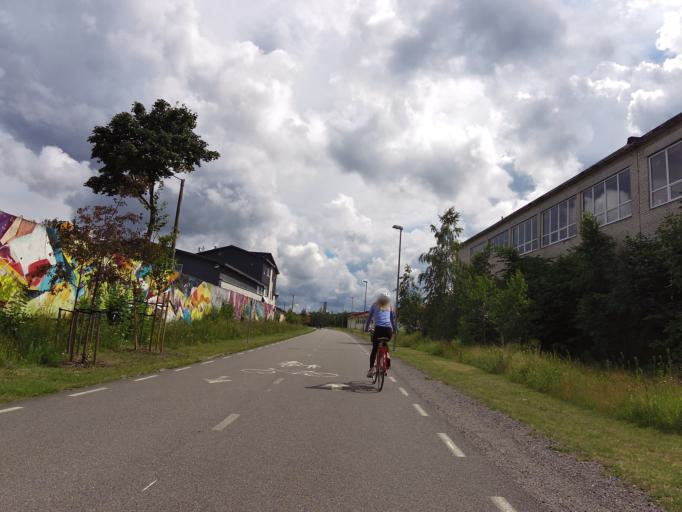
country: EE
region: Harju
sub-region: Saue vald
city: Laagri
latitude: 59.3828
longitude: 24.6604
